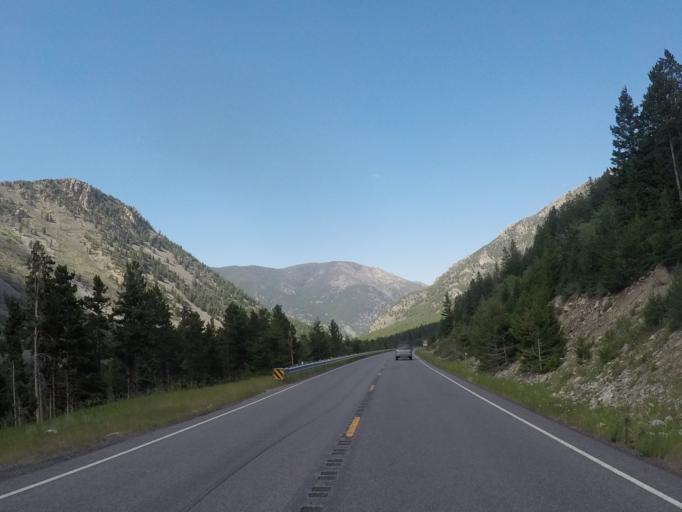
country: US
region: Montana
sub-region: Carbon County
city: Red Lodge
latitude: 45.0575
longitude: -109.4057
